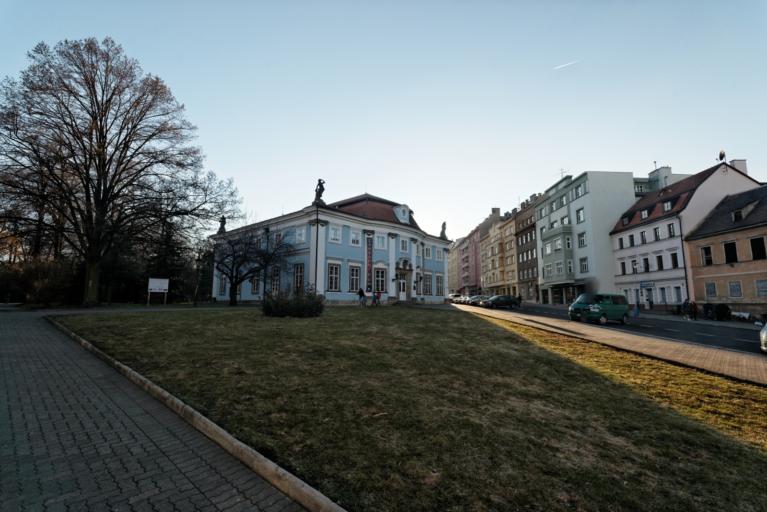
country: CZ
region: Ustecky
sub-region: Okres Teplice
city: Teplice
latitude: 50.6370
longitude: 13.8248
